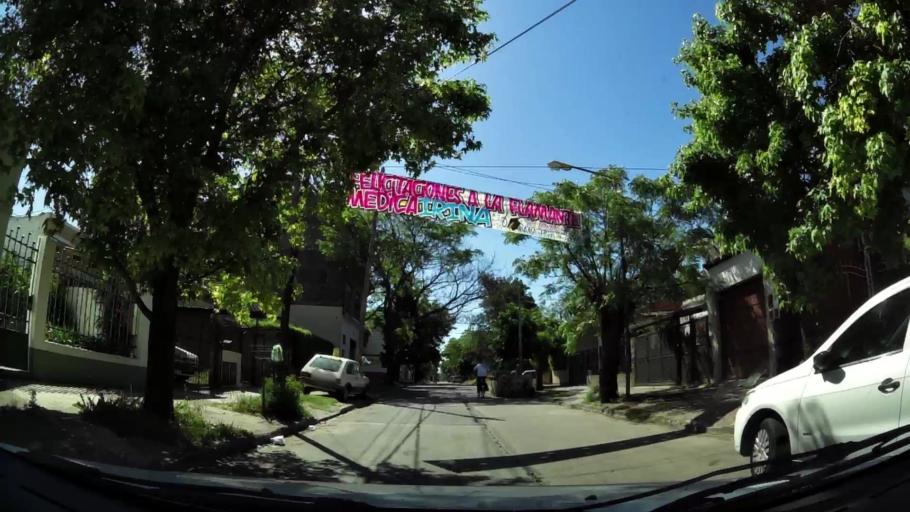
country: AR
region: Buenos Aires
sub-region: Partido de General San Martin
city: General San Martin
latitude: -34.5469
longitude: -58.5675
